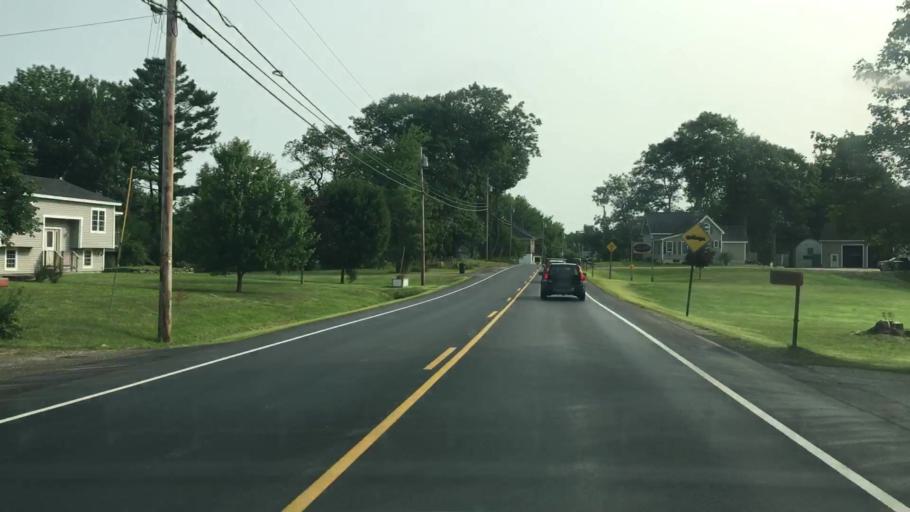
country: US
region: Maine
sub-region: Kennebec County
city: Chelsea
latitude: 44.2481
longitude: -69.7209
